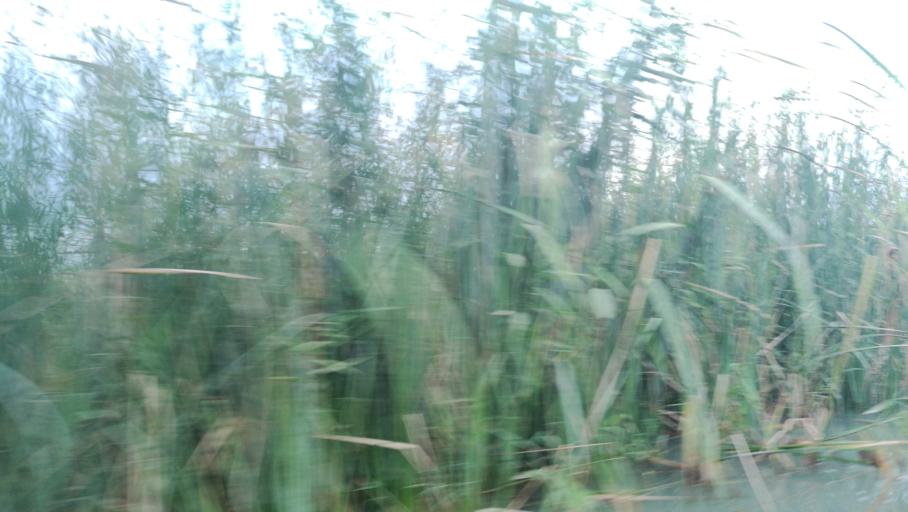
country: IQ
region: Dhi Qar
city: Al Jabayish
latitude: 30.9823
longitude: 47.0425
